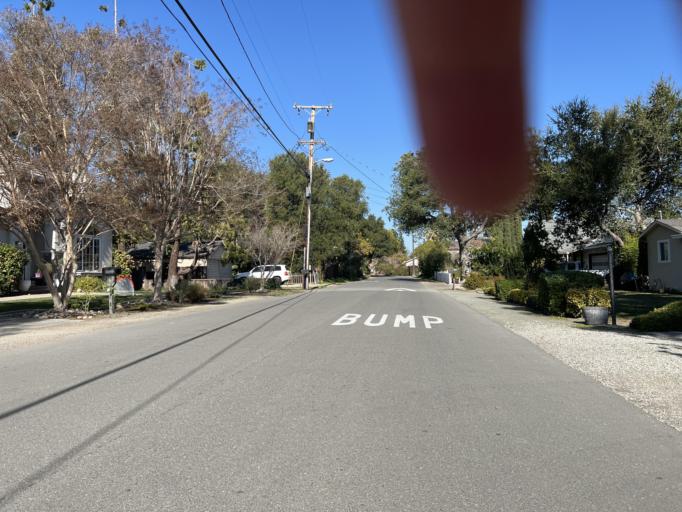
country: US
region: California
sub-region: Santa Clara County
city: Cupertino
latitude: 37.3159
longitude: -122.0650
